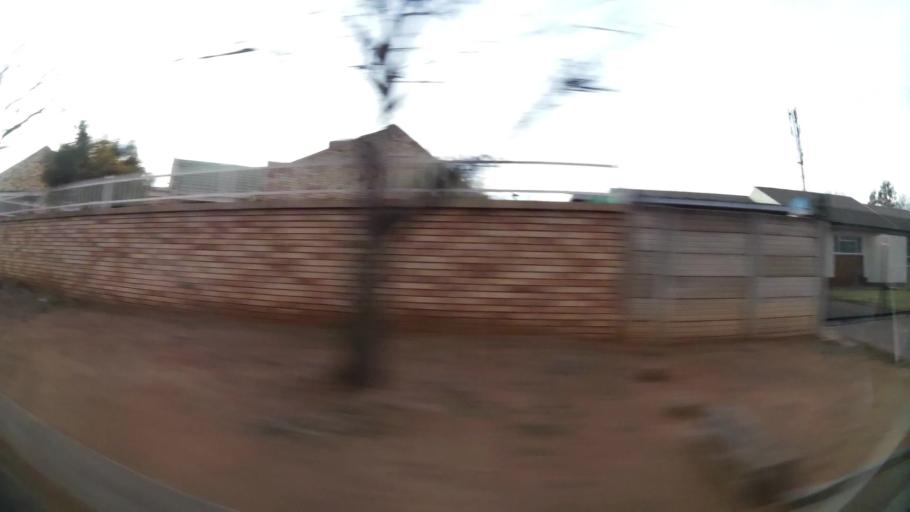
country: ZA
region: Orange Free State
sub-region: Mangaung Metropolitan Municipality
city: Bloemfontein
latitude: -29.1657
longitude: 26.1967
